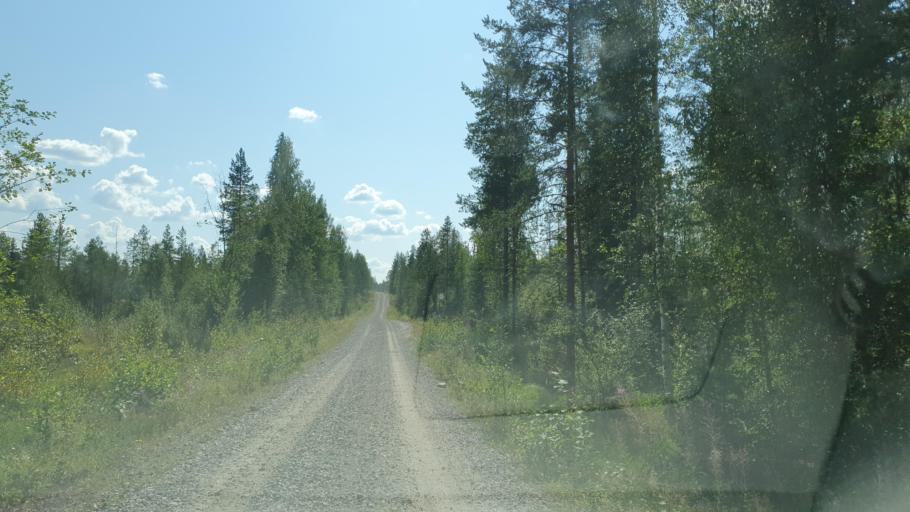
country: FI
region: Kainuu
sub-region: Kehys-Kainuu
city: Kuhmo
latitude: 63.9867
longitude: 29.5482
